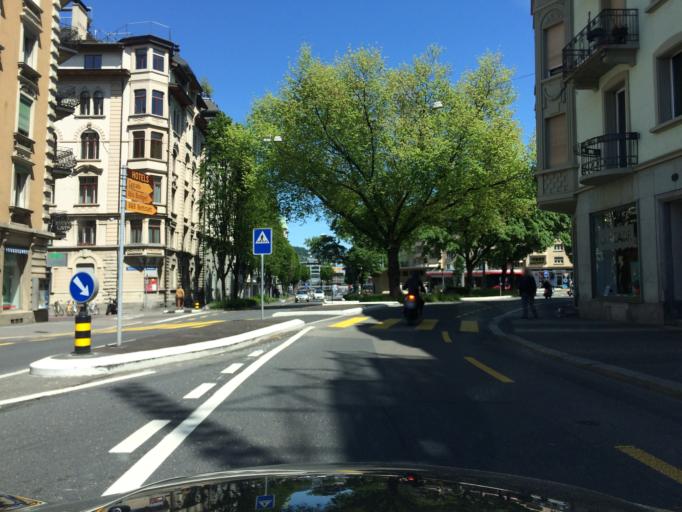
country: CH
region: Lucerne
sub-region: Lucerne-Stadt District
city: Luzern
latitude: 47.0453
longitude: 8.3076
